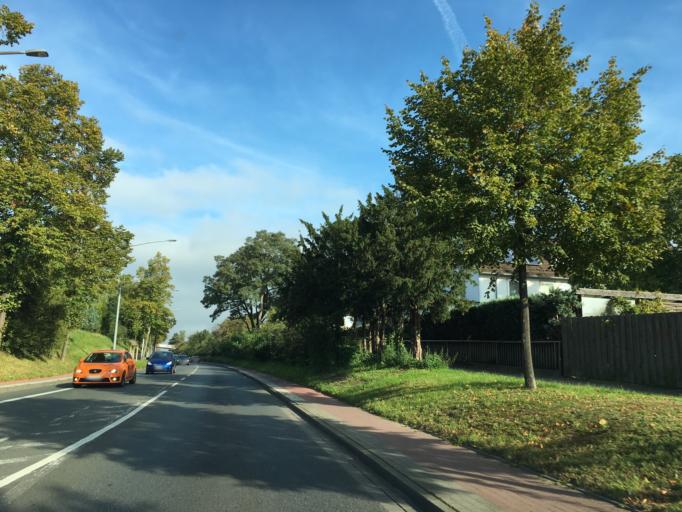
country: DE
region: Lower Saxony
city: Lueneburg
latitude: 53.2603
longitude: 10.4089
